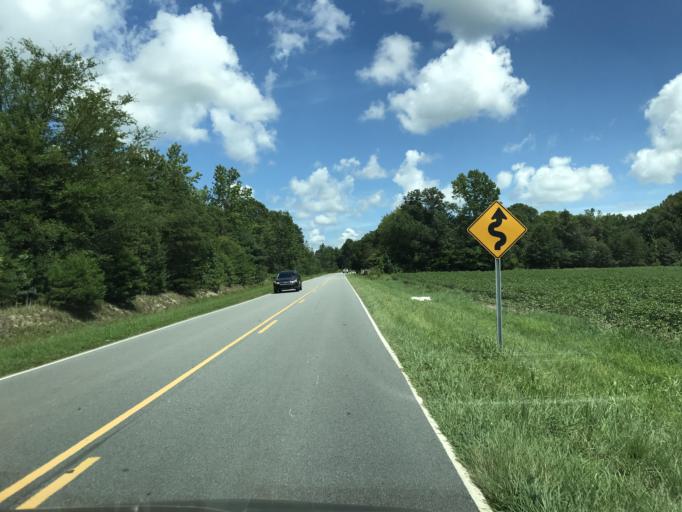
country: US
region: North Carolina
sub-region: Lincoln County
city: Lincolnton
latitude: 35.5050
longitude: -81.2206
